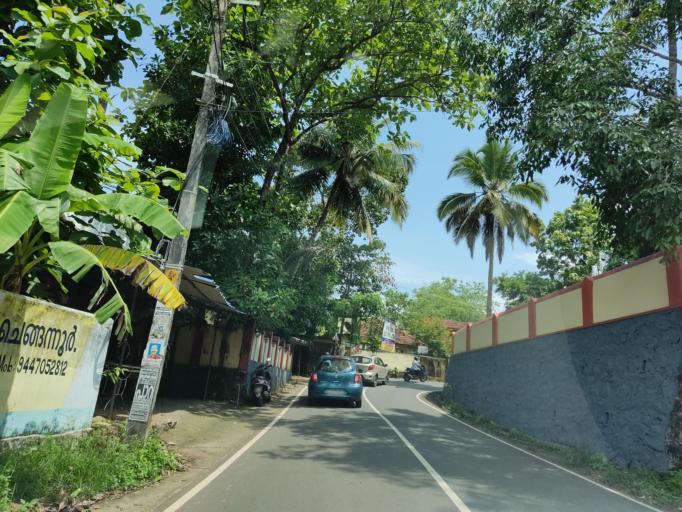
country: IN
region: Kerala
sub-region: Alappuzha
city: Chengannur
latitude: 9.3019
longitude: 76.5865
